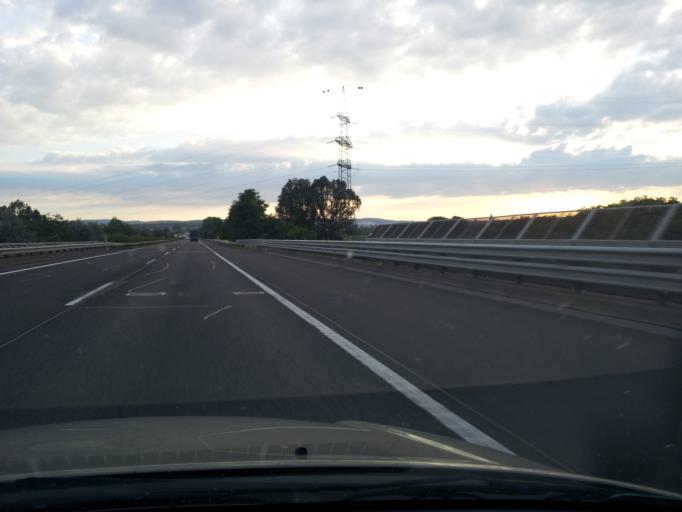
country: HU
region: Pest
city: Hevizgyoerk
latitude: 47.6416
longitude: 19.5138
